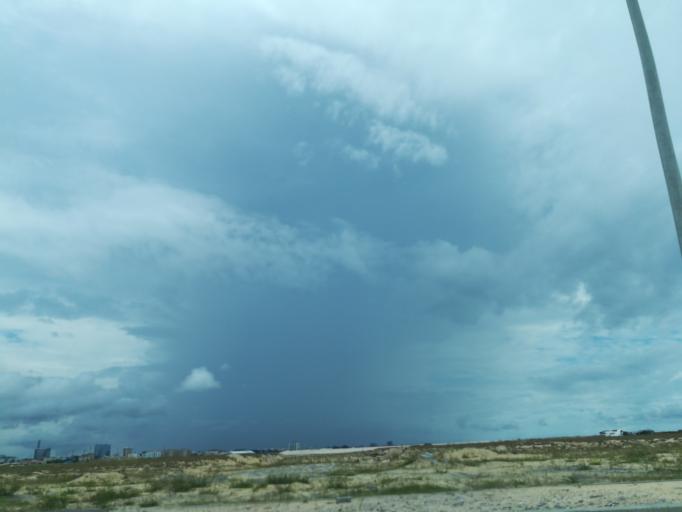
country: NG
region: Lagos
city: Ikoyi
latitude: 6.4140
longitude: 3.4251
